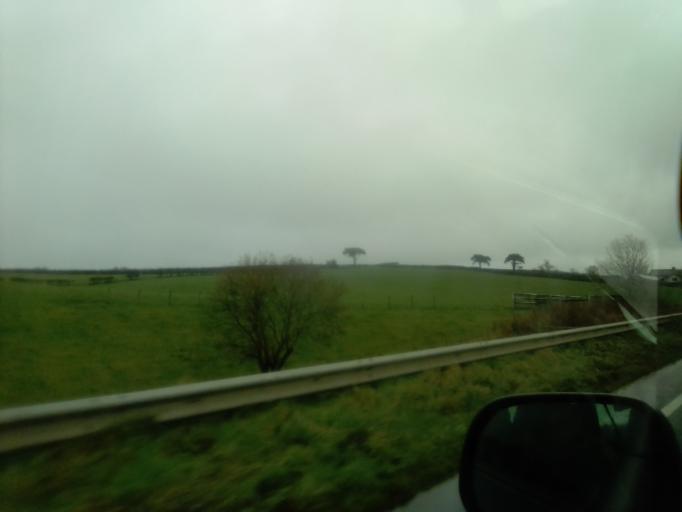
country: GB
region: Northern Ireland
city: Newtownstewart
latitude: 54.7231
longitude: -7.3788
